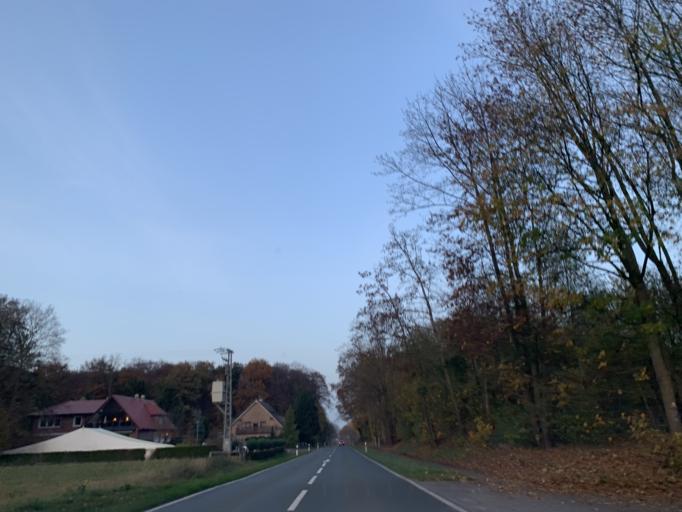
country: DE
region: North Rhine-Westphalia
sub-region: Regierungsbezirk Munster
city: Nottuln
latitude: 51.9743
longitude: 7.3465
